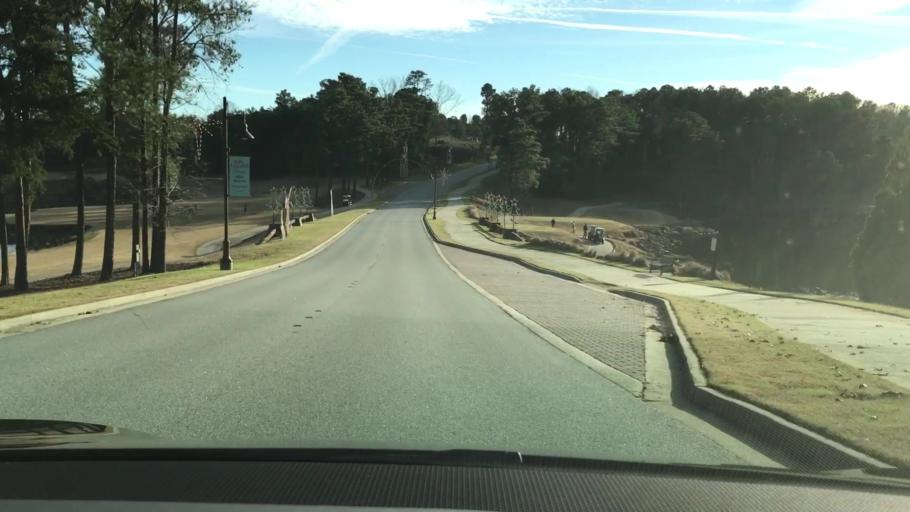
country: US
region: Georgia
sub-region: Gwinnett County
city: Buford
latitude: 34.1843
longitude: -84.0186
